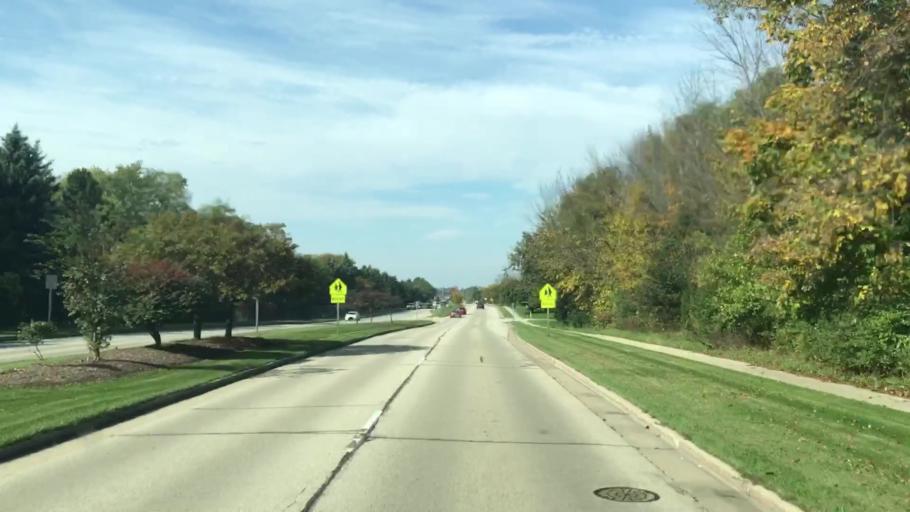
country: US
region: Wisconsin
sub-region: Ozaukee County
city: Thiensville
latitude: 43.2216
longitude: -87.9662
